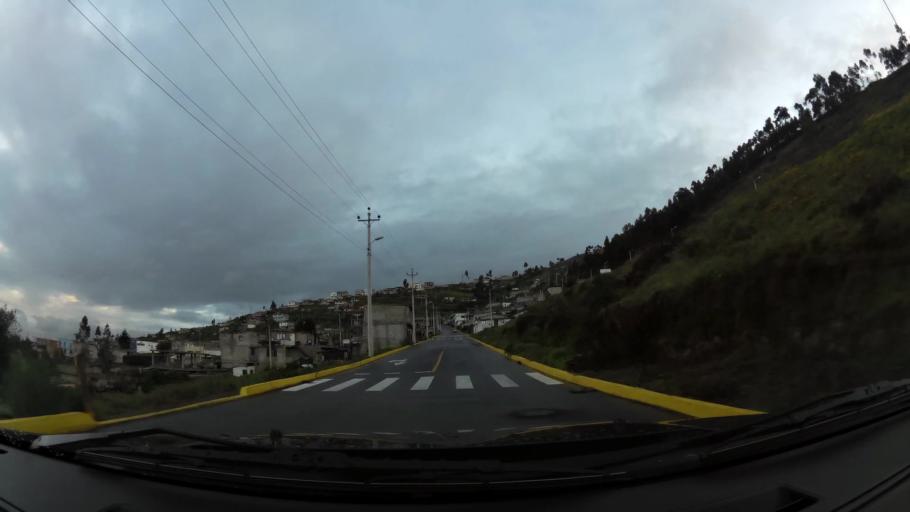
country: EC
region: Pichincha
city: Quito
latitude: -0.0937
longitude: -78.5305
